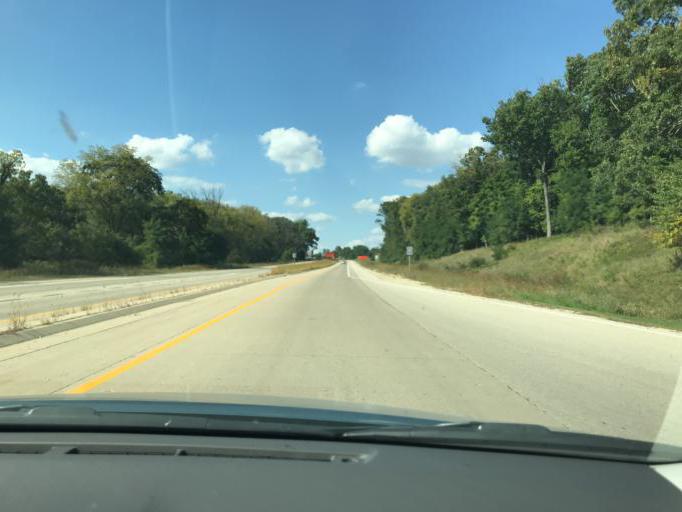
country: US
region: Wisconsin
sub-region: Walworth County
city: Williams Bay
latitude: 42.5941
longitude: -88.5355
